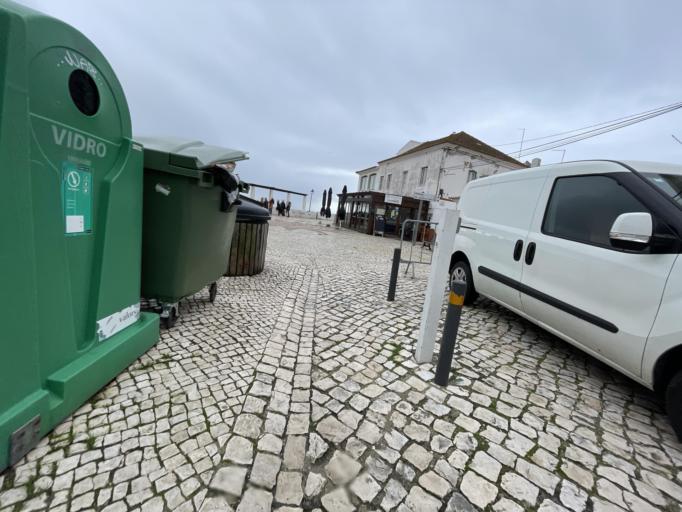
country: PT
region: Leiria
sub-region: Nazare
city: Nazare
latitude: 39.6052
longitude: -9.0742
